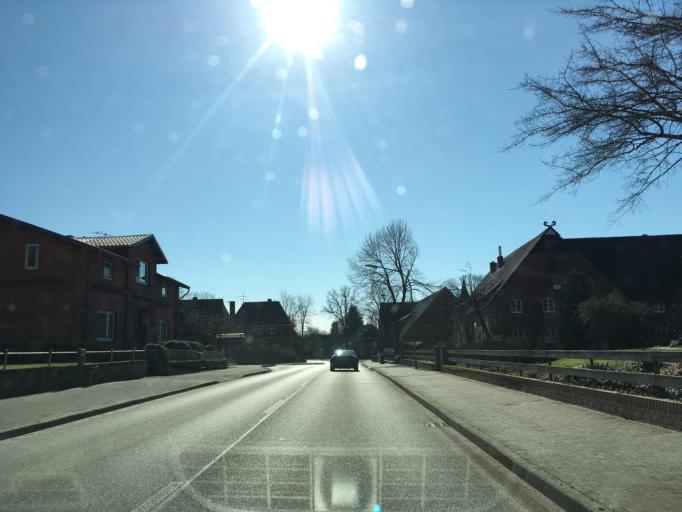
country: DE
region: Schleswig-Holstein
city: Berkenthin
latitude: 53.7324
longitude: 10.6509
